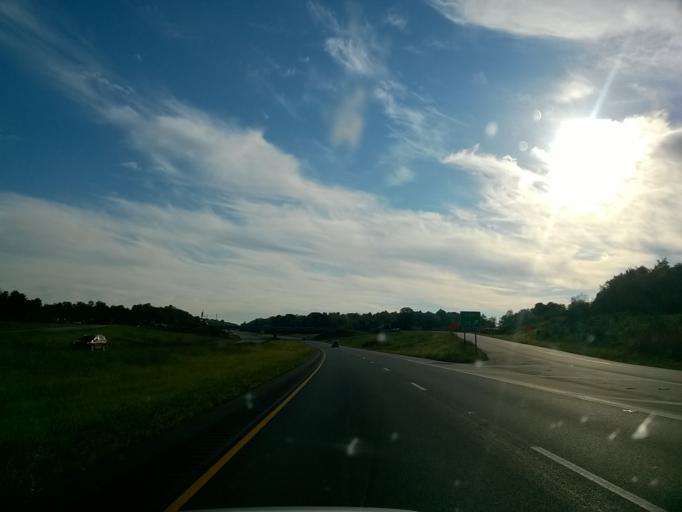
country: US
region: Indiana
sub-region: Warrick County
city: Boonville
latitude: 38.1930
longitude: -87.2961
